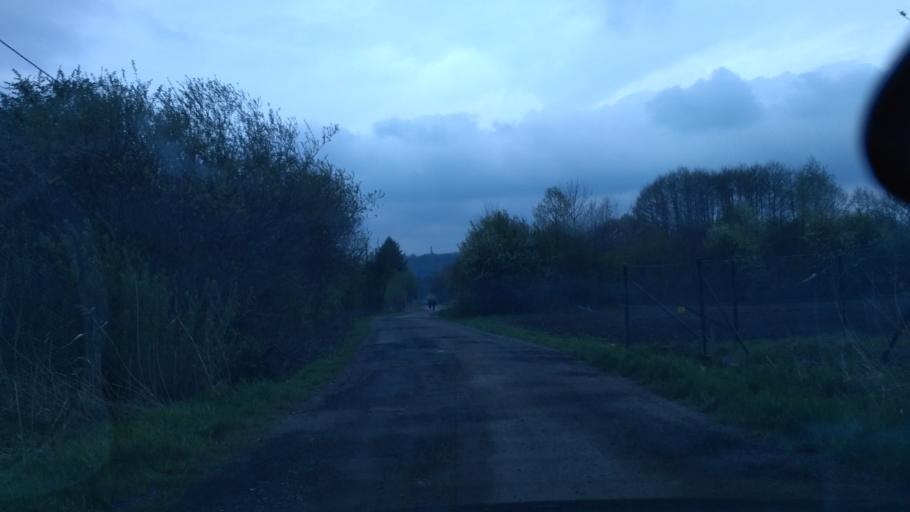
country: PL
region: Subcarpathian Voivodeship
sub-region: Powiat sanocki
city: Sanok
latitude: 49.5698
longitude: 22.2179
